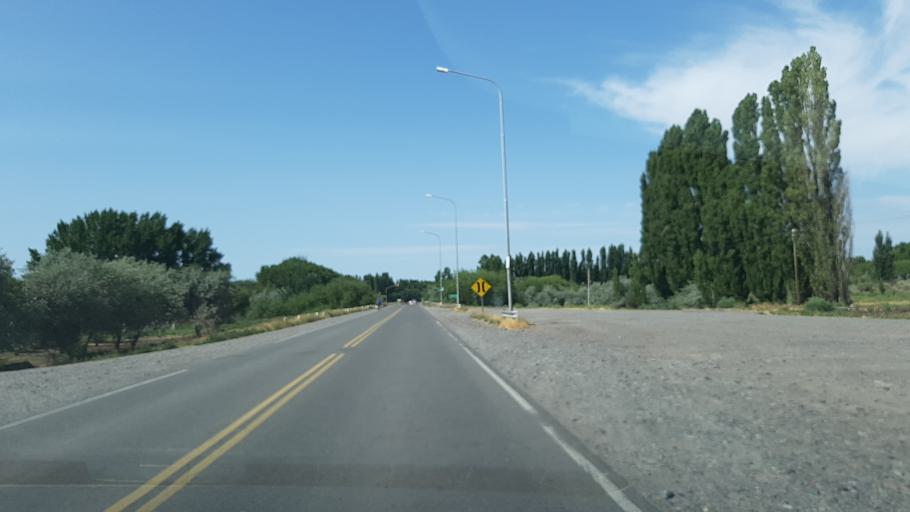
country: AR
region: Neuquen
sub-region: Departamento de Picun Leufu
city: Picun Leufu
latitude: -39.5228
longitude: -69.2968
